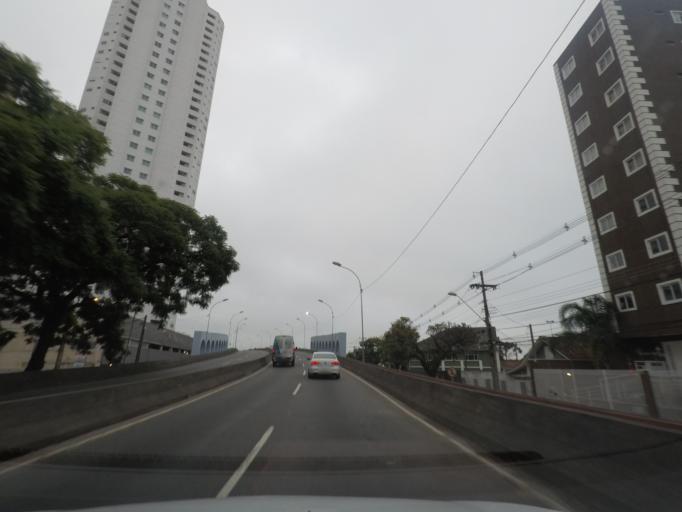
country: BR
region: Parana
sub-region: Curitiba
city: Curitiba
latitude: -25.4348
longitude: -49.2549
